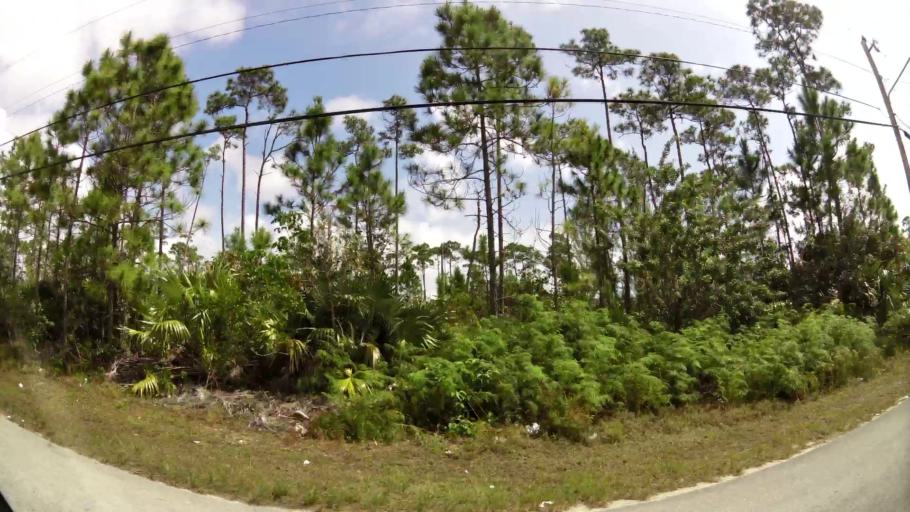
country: BS
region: Freeport
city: Lucaya
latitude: 26.5383
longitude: -78.6316
